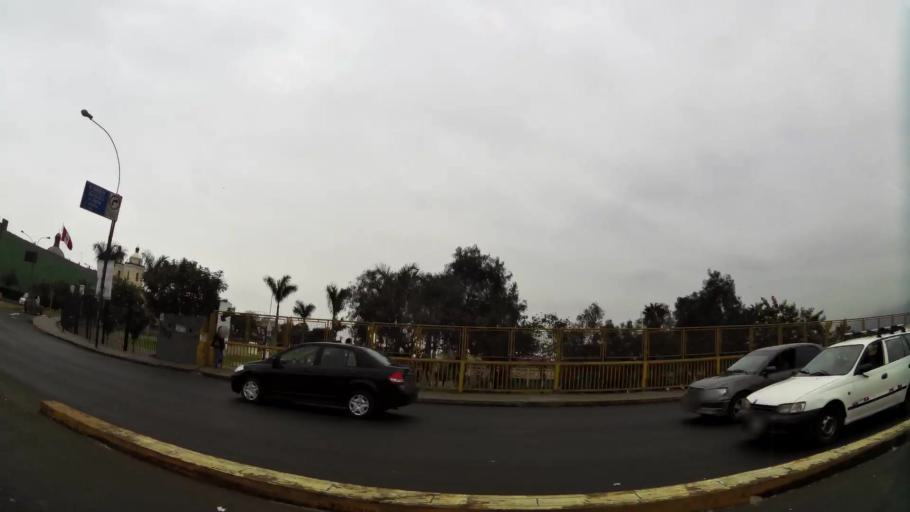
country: PE
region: Lima
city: Lima
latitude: -12.0446
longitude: -77.0250
